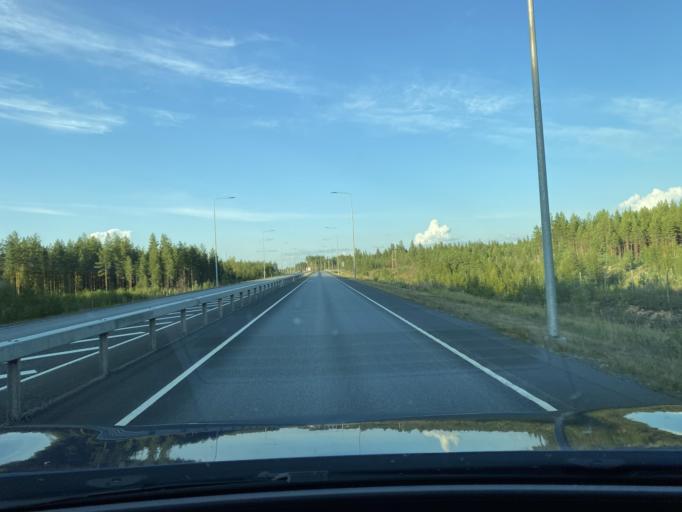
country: FI
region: Southern Ostrobothnia
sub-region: Seinaejoki
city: Seinaejoki
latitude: 62.7108
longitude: 22.8422
